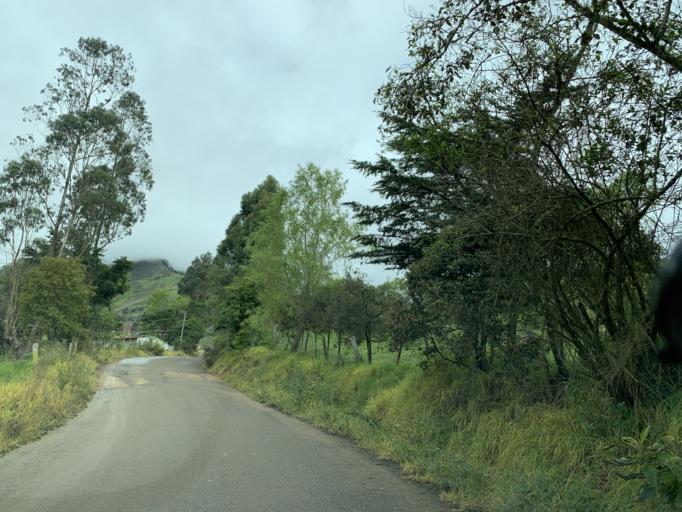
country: CO
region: Boyaca
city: Tibana
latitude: 5.3124
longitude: -73.4247
